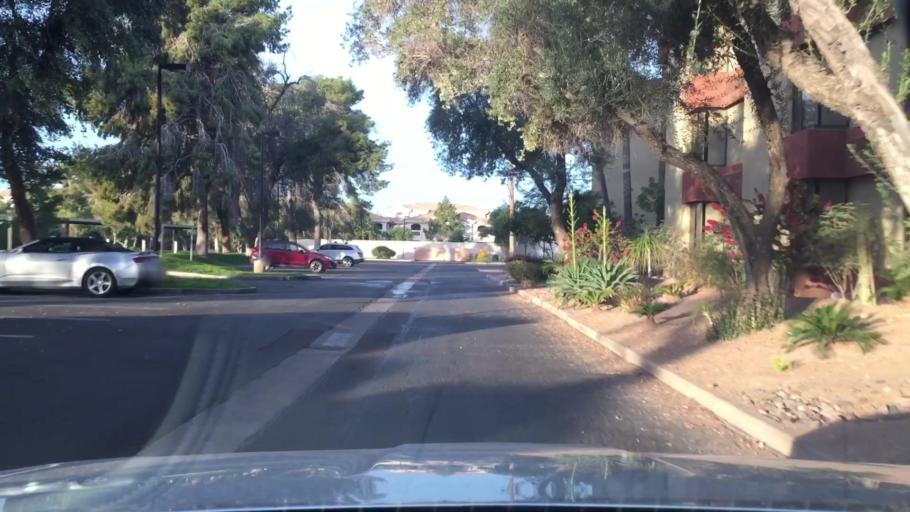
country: US
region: Arizona
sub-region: Maricopa County
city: Tempe Junction
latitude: 33.4058
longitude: -111.9624
